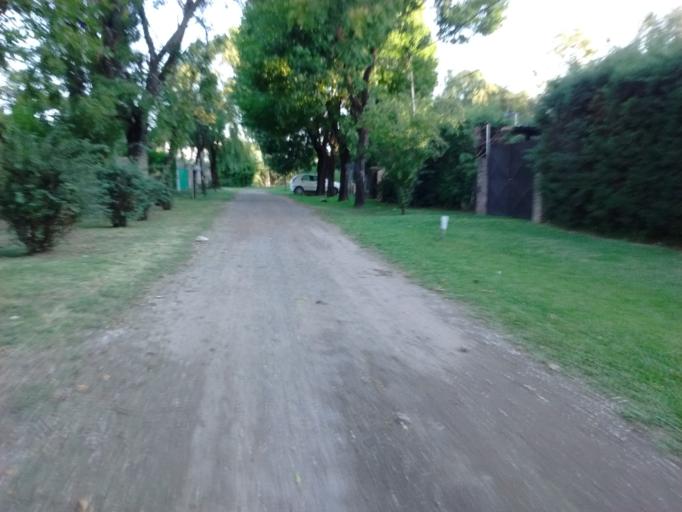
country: AR
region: Santa Fe
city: Funes
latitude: -32.9231
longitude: -60.8259
